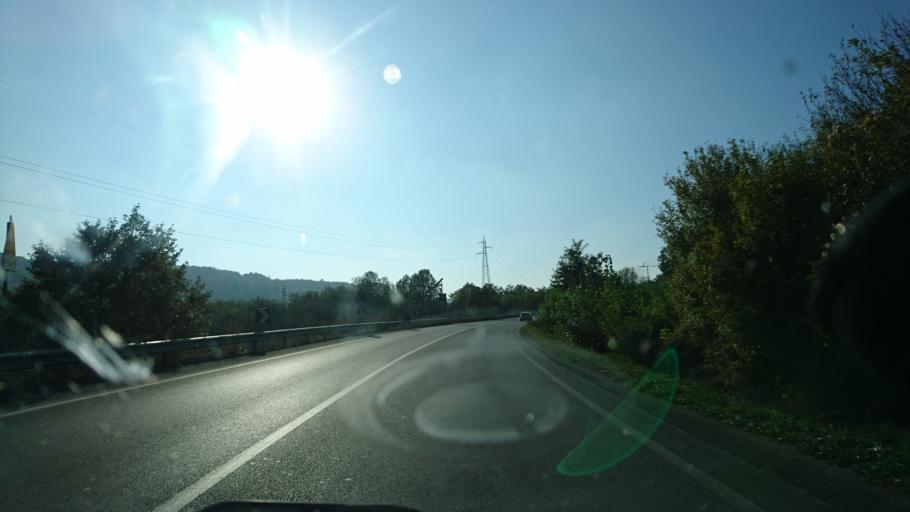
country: IT
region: Piedmont
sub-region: Provincia di Alessandria
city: Bistagno
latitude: 44.6573
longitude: 8.3921
